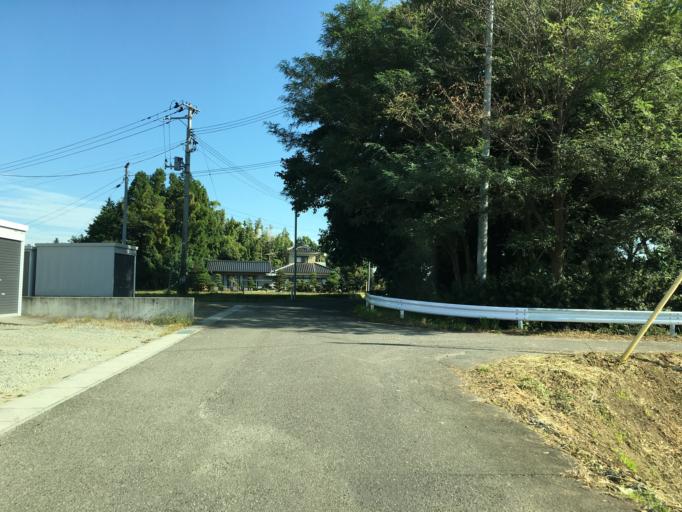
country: JP
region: Fukushima
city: Motomiya
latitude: 37.5409
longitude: 140.3717
